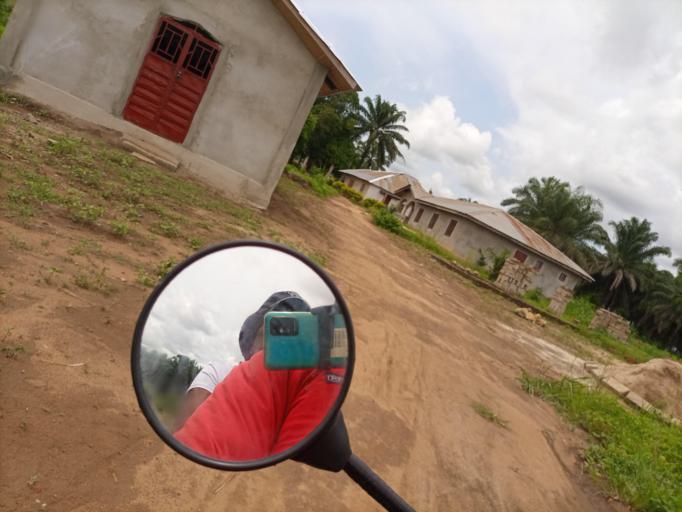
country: SL
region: Southern Province
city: Bo
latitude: 7.9640
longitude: -11.7168
